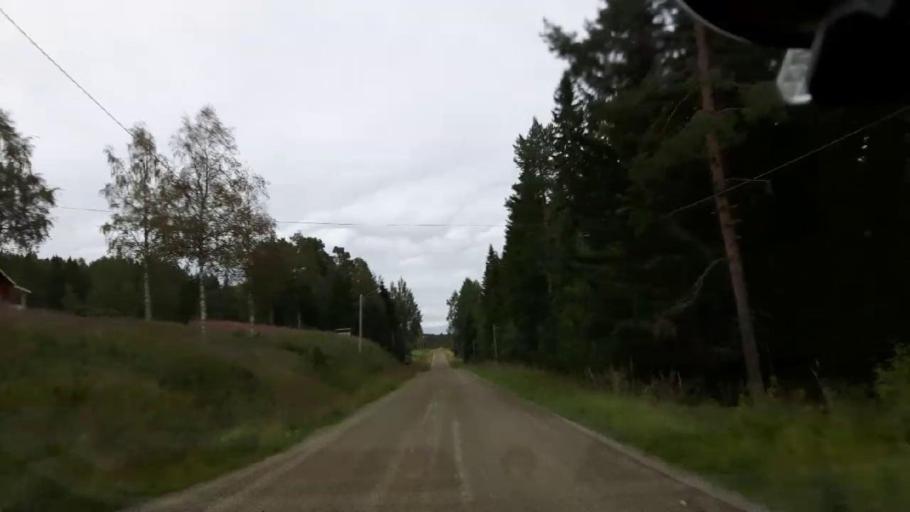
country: SE
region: Jaemtland
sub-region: Braecke Kommun
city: Braecke
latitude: 63.0376
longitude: 15.3629
